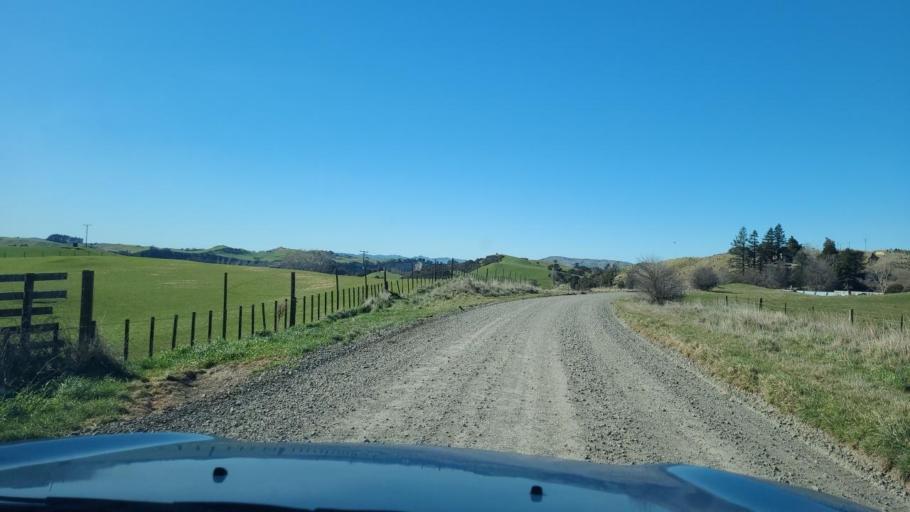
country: NZ
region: Hawke's Bay
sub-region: Napier City
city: Taradale
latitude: -39.4455
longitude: 176.5493
